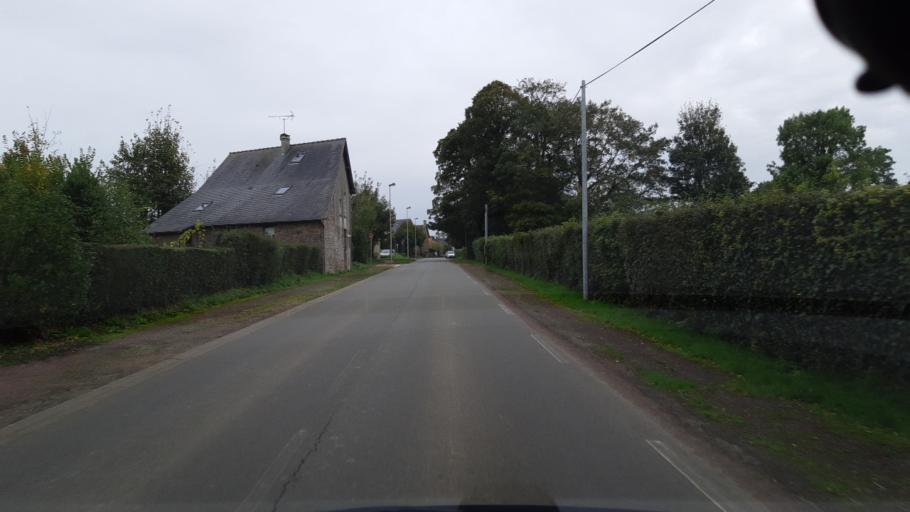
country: FR
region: Lower Normandy
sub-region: Departement de la Manche
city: Hambye
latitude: 48.9509
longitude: -1.2647
